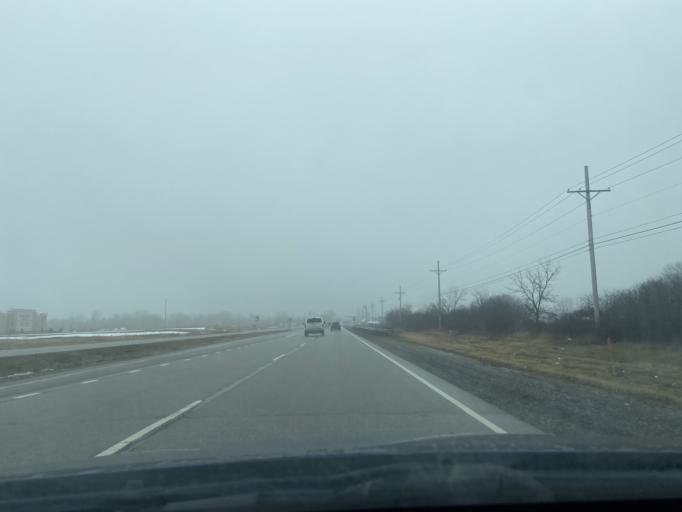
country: US
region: Illinois
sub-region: Lake County
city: Volo
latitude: 42.3183
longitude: -88.1647
